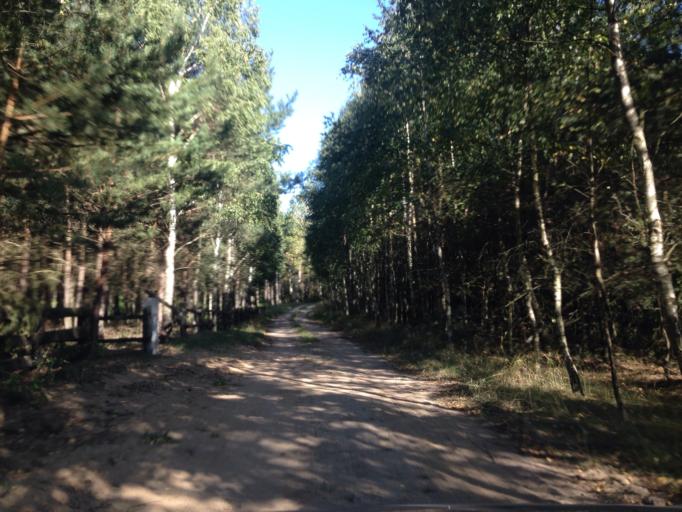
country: PL
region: Kujawsko-Pomorskie
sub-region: Powiat brodnicki
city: Gorzno
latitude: 53.1537
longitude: 19.6584
